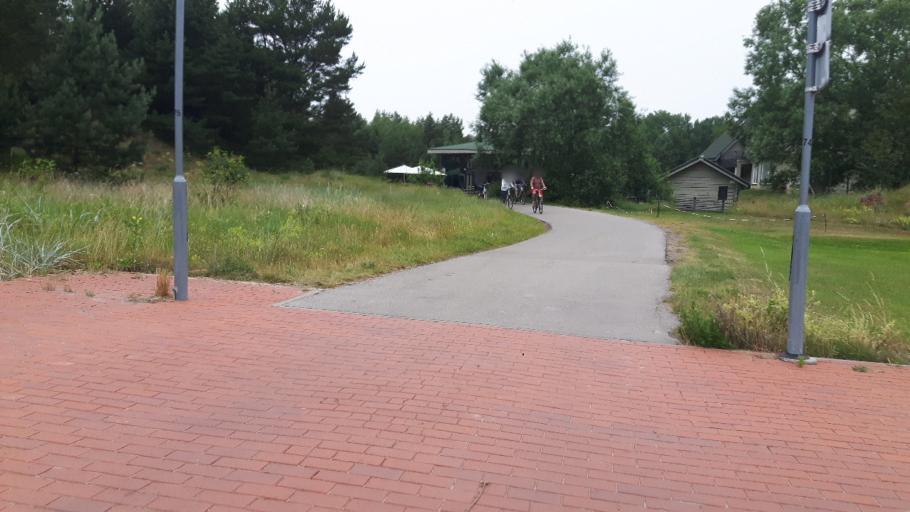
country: LT
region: Klaipedos apskritis
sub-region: Palanga
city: Sventoji
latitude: 56.0168
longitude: 21.0760
